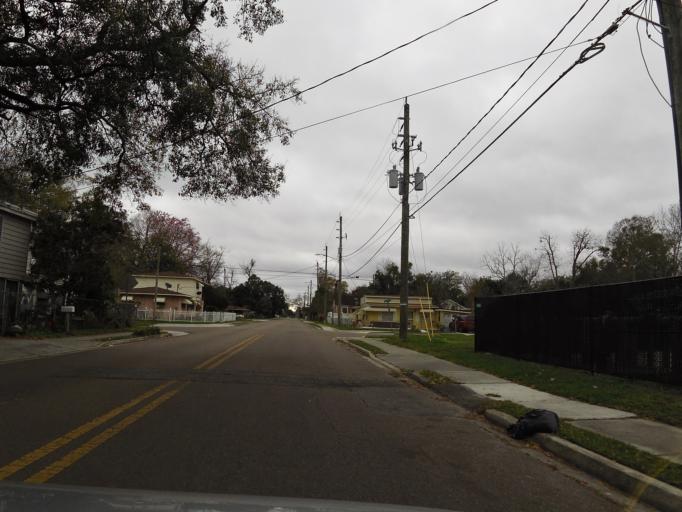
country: US
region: Florida
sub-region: Duval County
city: Jacksonville
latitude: 30.3597
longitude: -81.6865
